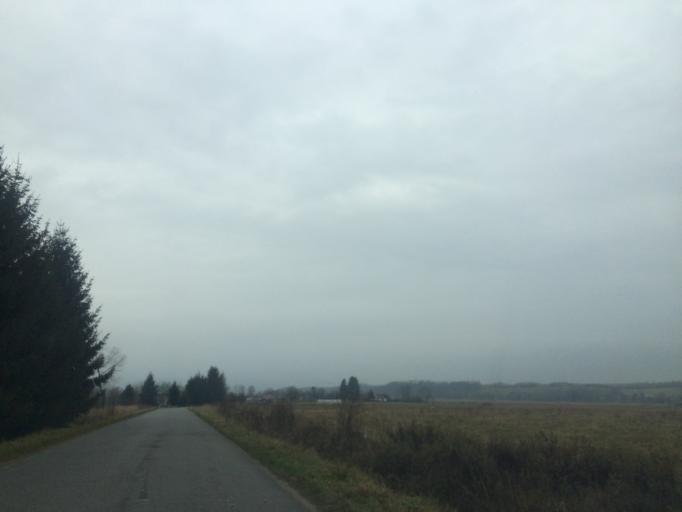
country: PL
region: Lower Silesian Voivodeship
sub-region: Powiat klodzki
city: Bystrzyca Klodzka
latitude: 50.2368
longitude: 16.7199
